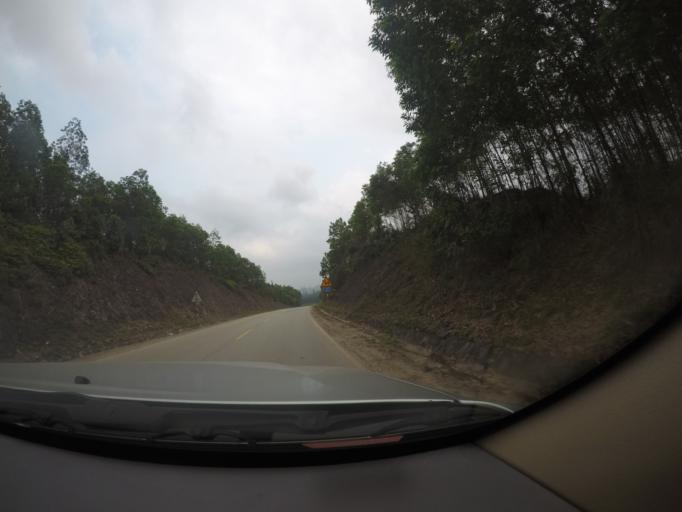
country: VN
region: Quang Binh
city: Kien Giang
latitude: 17.1292
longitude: 106.7801
